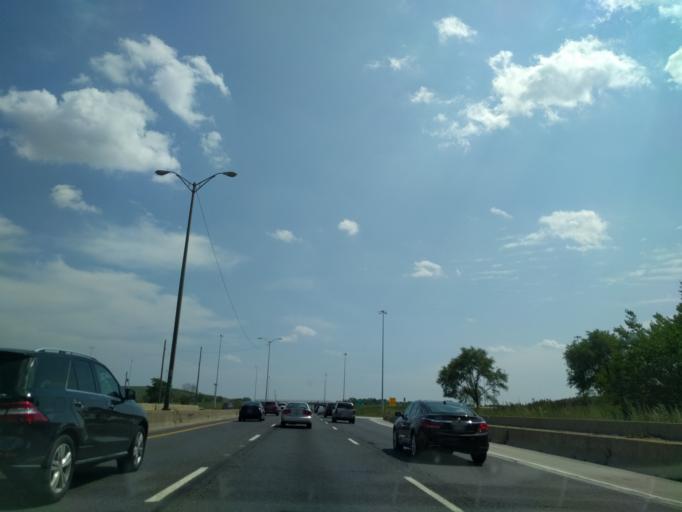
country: US
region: Illinois
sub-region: Cook County
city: Dolton
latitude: 41.6632
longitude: -87.5917
